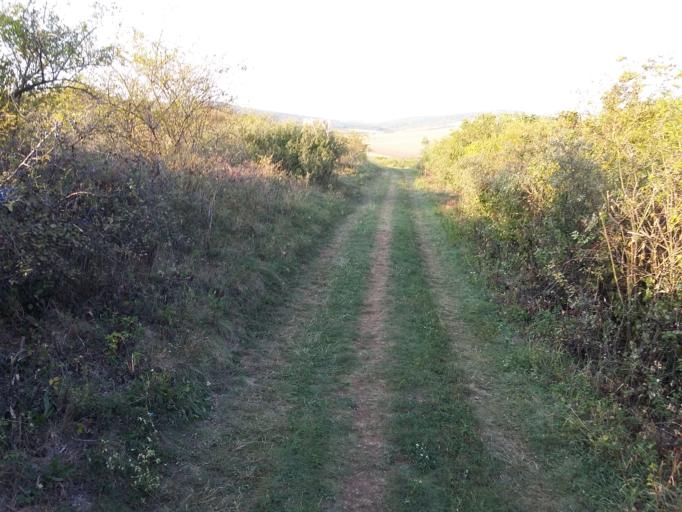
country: HU
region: Borsod-Abauj-Zemplen
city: Bekecs
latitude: 48.1576
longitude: 21.1727
